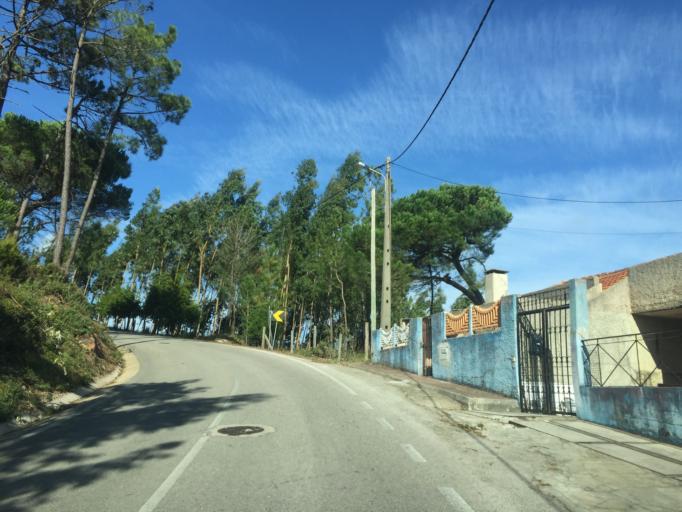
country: PT
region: Coimbra
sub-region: Figueira da Foz
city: Tavarede
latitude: 40.1779
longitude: -8.8374
